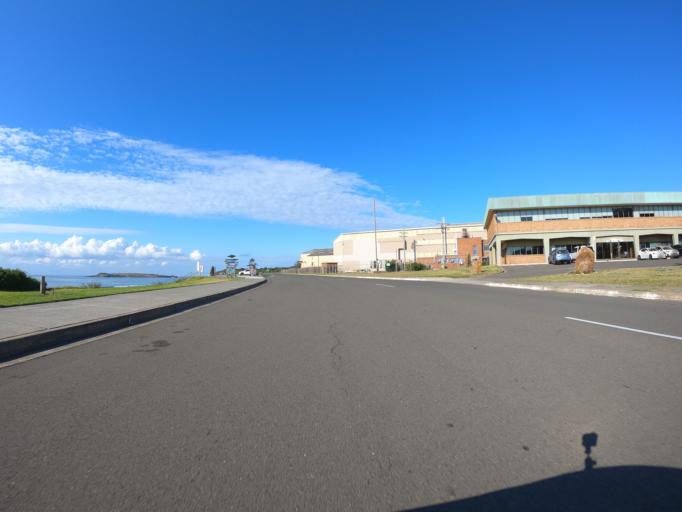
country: AU
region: New South Wales
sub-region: Wollongong
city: Port Kembla
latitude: -34.4822
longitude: 150.9131
